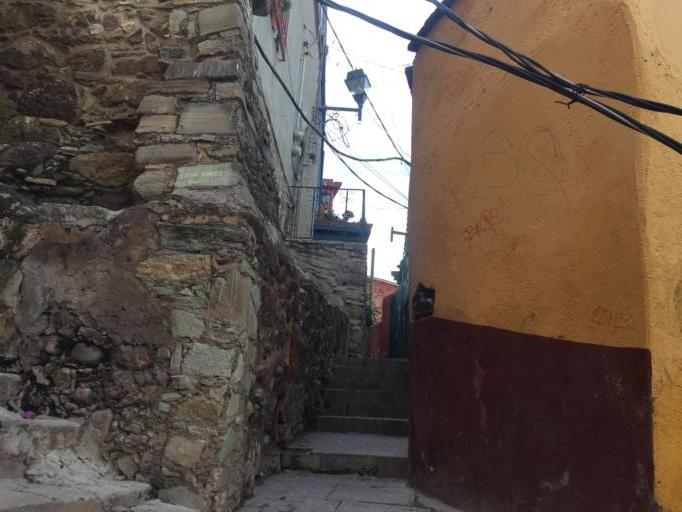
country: MX
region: Guanajuato
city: Guanajuato
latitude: 21.0155
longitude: -101.2546
